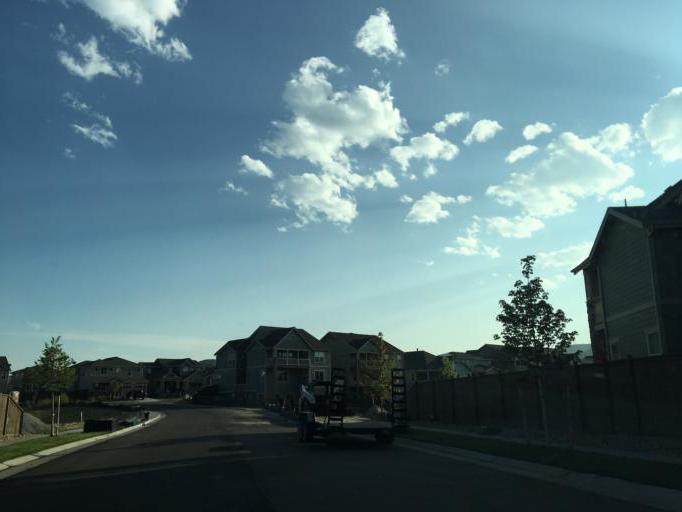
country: US
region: Colorado
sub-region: Jefferson County
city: Applewood
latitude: 39.7862
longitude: -105.1710
